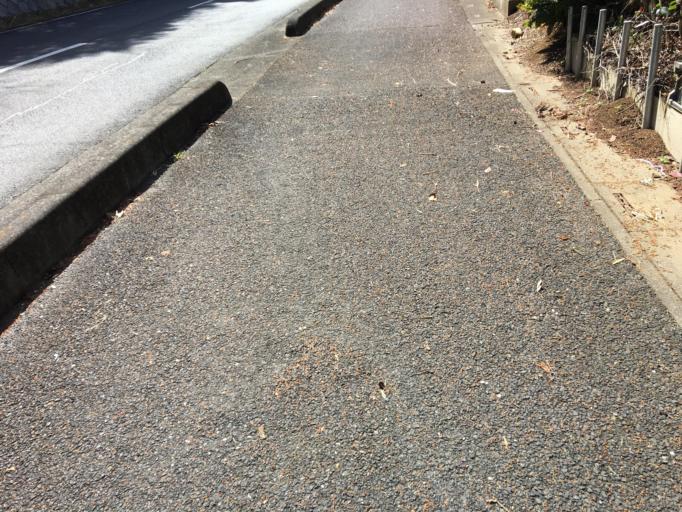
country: JP
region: Saitama
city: Ogawa
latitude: 36.0242
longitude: 139.3298
